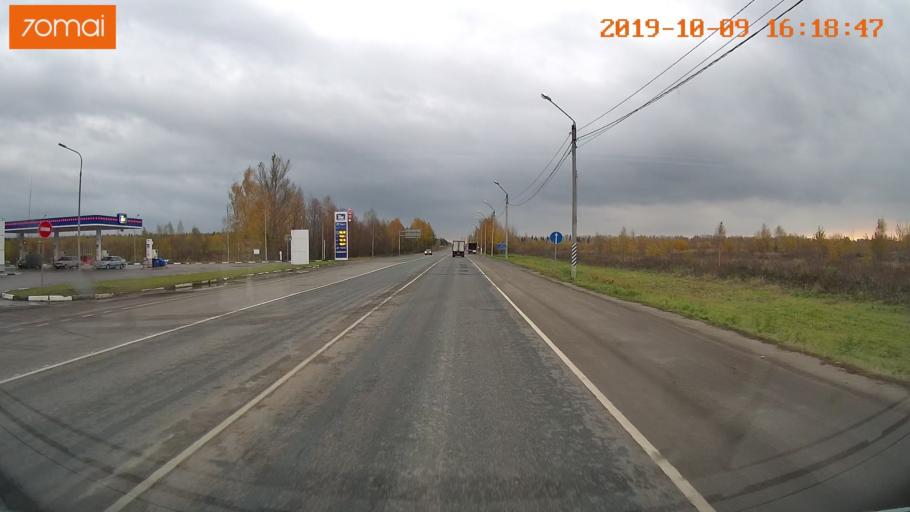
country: RU
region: Kostroma
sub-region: Kostromskoy Rayon
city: Kostroma
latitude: 57.7256
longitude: 40.8961
